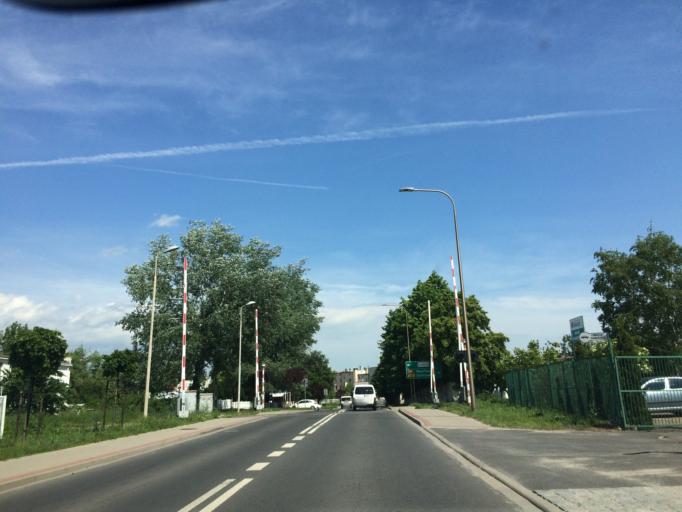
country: PL
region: Lower Silesian Voivodeship
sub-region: Powiat swidnicki
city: Swidnica
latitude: 50.8330
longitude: 16.4998
